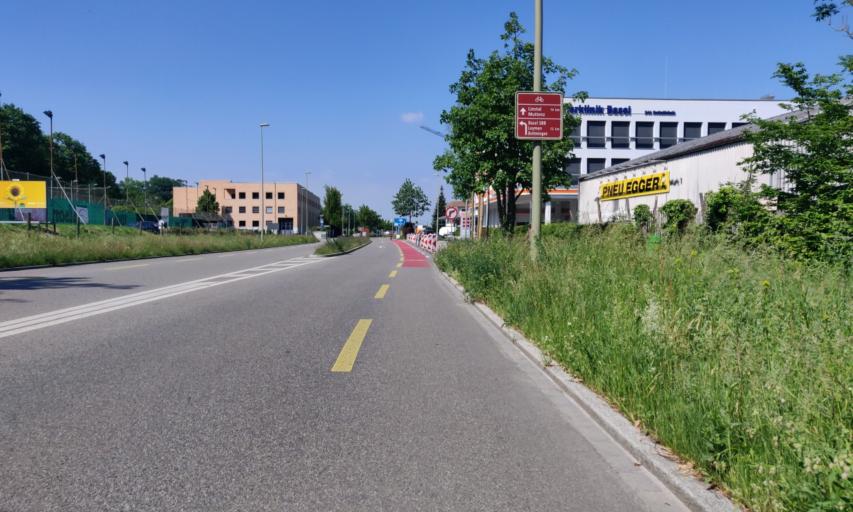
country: CH
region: Basel-Landschaft
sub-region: Bezirk Arlesheim
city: Munchenstein
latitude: 47.5237
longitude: 7.6039
